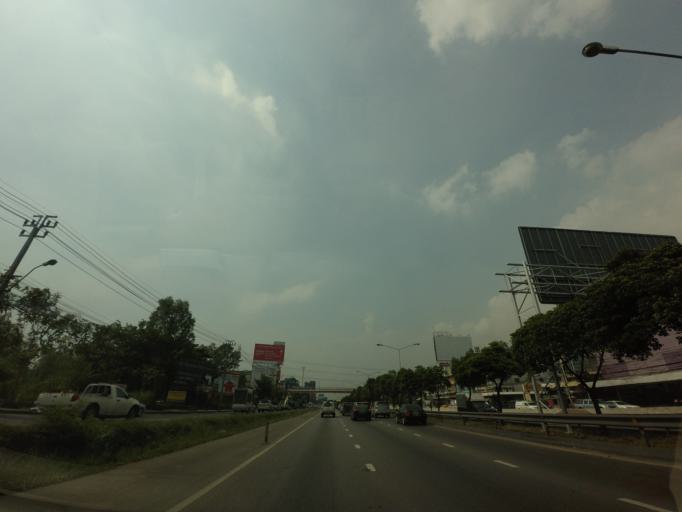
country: TH
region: Bangkok
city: Thawi Watthana
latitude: 13.7871
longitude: 100.3689
